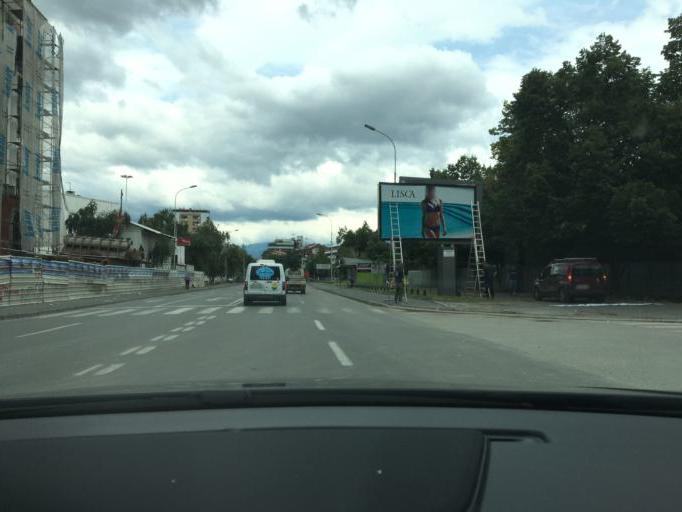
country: MK
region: Karpos
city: Skopje
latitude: 41.9969
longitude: 21.4380
